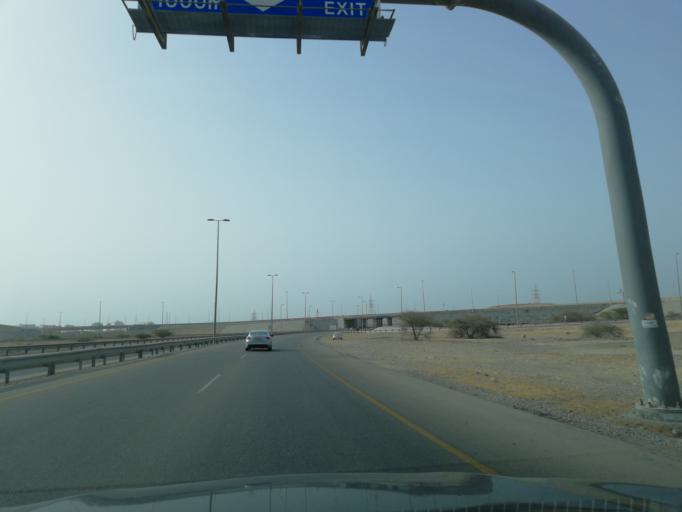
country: OM
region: Muhafazat Masqat
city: As Sib al Jadidah
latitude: 23.5629
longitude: 58.1898
